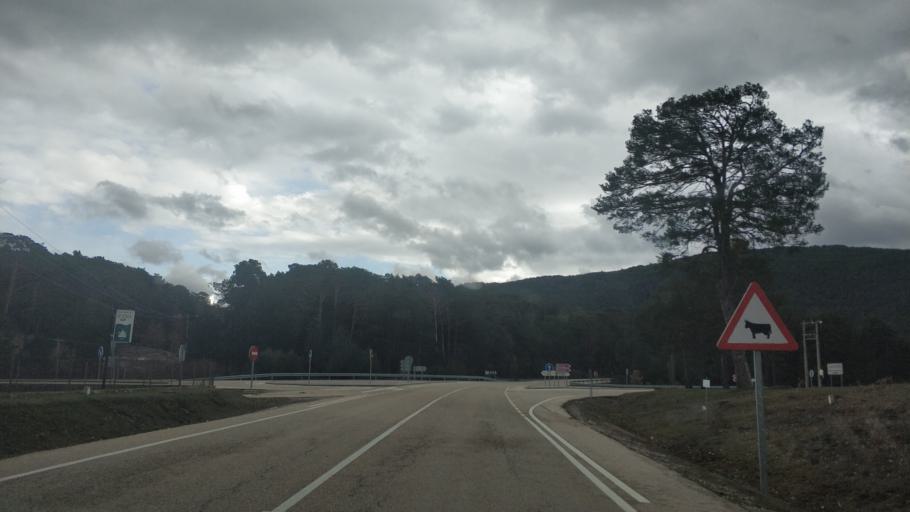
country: ES
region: Castille and Leon
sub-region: Provincia de Burgos
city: Regumiel de la Sierra
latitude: 41.9571
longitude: -3.0144
